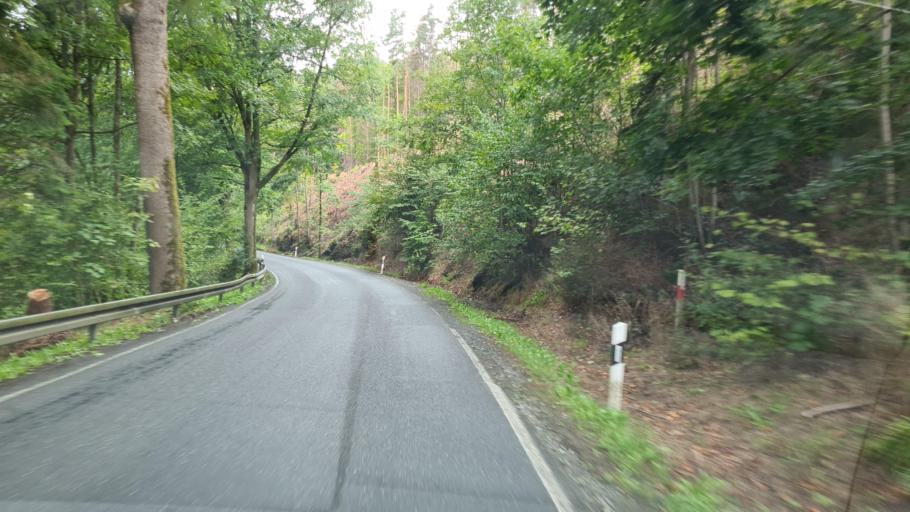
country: DE
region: Thuringia
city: Leutenberg
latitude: 50.5345
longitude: 11.4943
